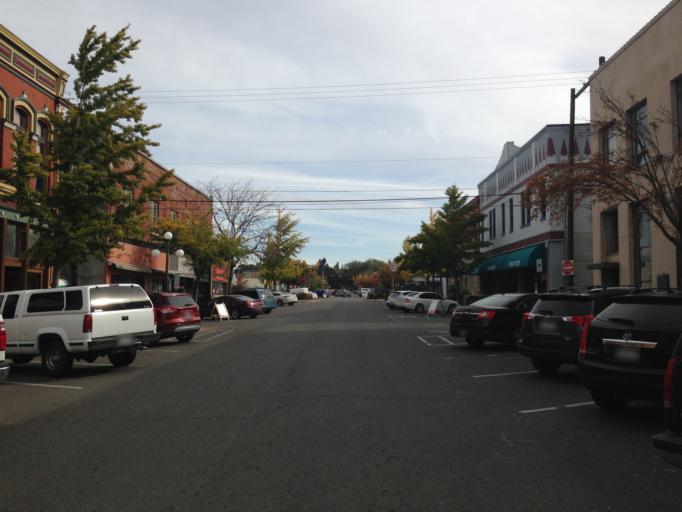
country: US
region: Washington
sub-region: Kittitas County
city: Ellensburg
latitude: 46.9955
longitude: -120.5471
